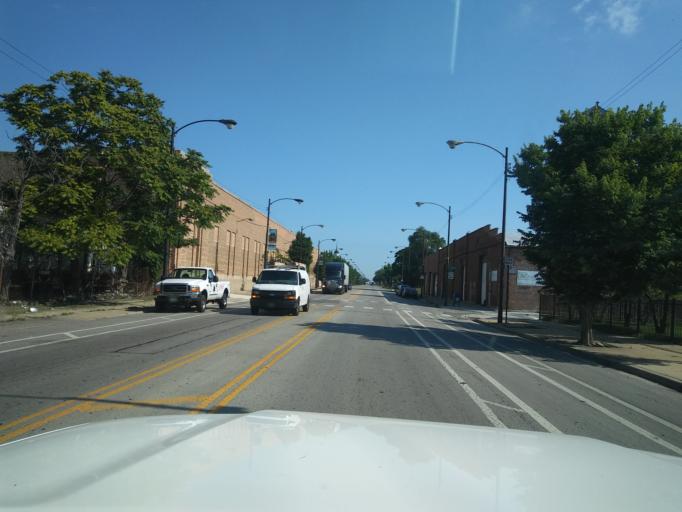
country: US
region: Illinois
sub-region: Cook County
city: Chicago
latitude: 41.8131
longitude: -87.6456
